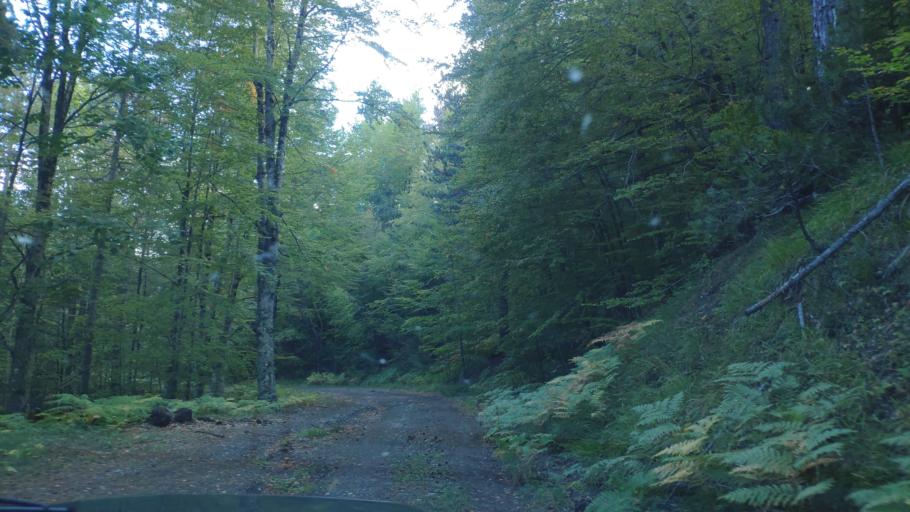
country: AL
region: Korce
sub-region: Rrethi i Devollit
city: Miras
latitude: 40.3460
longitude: 20.8993
